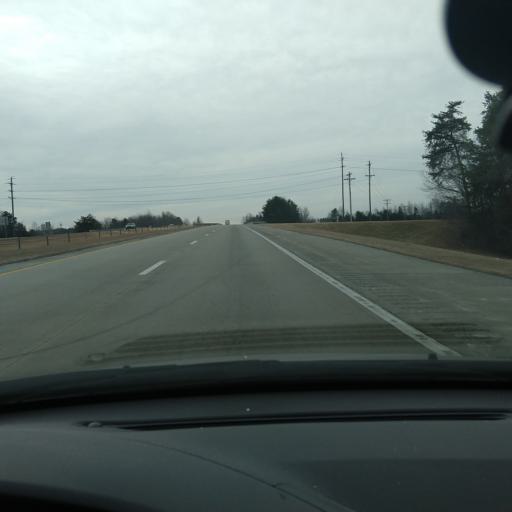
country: US
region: North Carolina
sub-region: Davidson County
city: Midway
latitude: 35.9399
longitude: -80.2346
